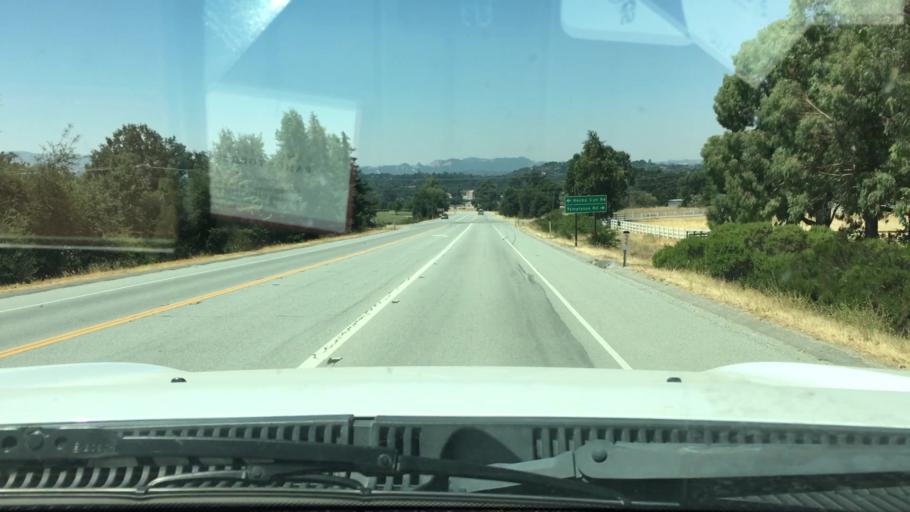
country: US
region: California
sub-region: San Luis Obispo County
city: Atascadero
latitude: 35.5049
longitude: -120.6507
